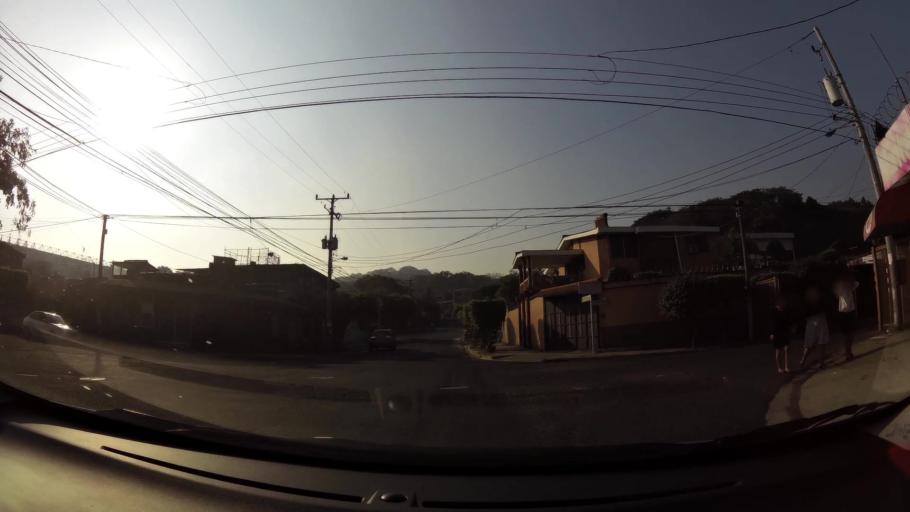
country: SV
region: La Libertad
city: Antiguo Cuscatlan
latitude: 13.6822
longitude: -89.2248
